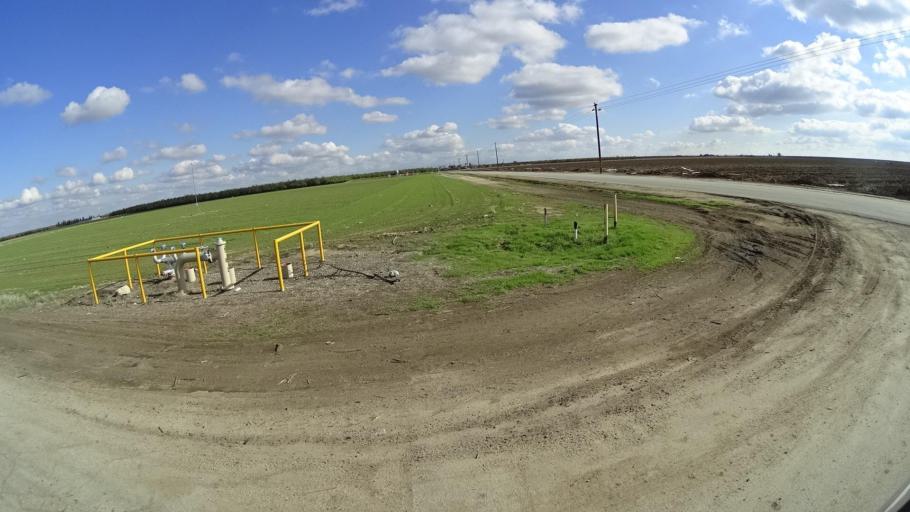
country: US
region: California
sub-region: Kern County
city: McFarland
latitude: 35.6746
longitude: -119.2672
